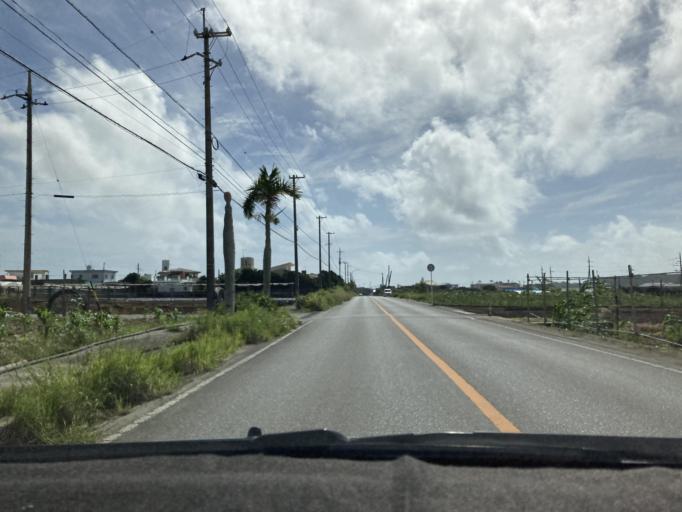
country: JP
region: Okinawa
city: Itoman
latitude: 26.1015
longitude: 127.6722
